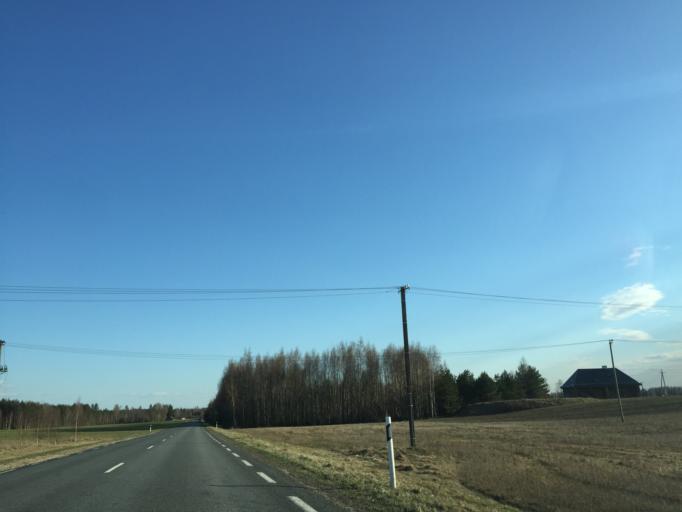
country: EE
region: Valgamaa
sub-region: Torva linn
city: Torva
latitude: 58.1346
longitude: 25.9904
